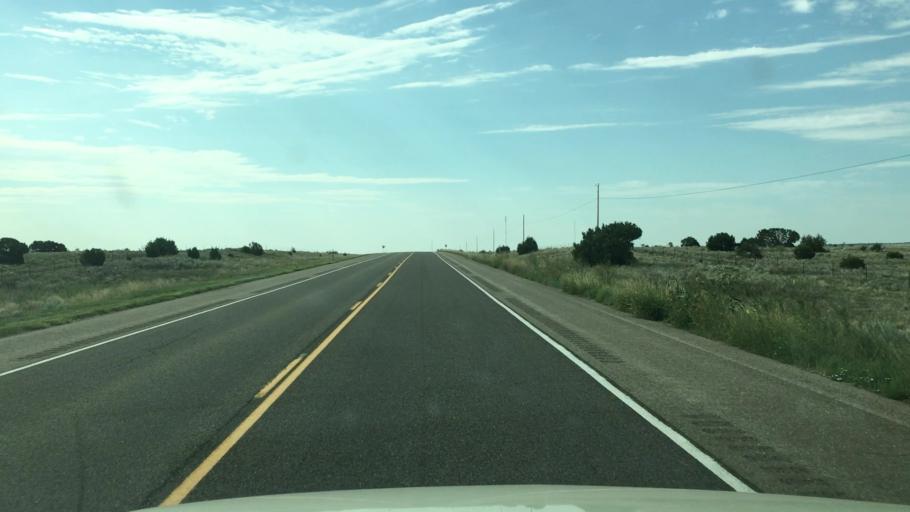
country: US
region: New Mexico
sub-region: Torrance County
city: Moriarty
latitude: 35.0290
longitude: -105.6759
